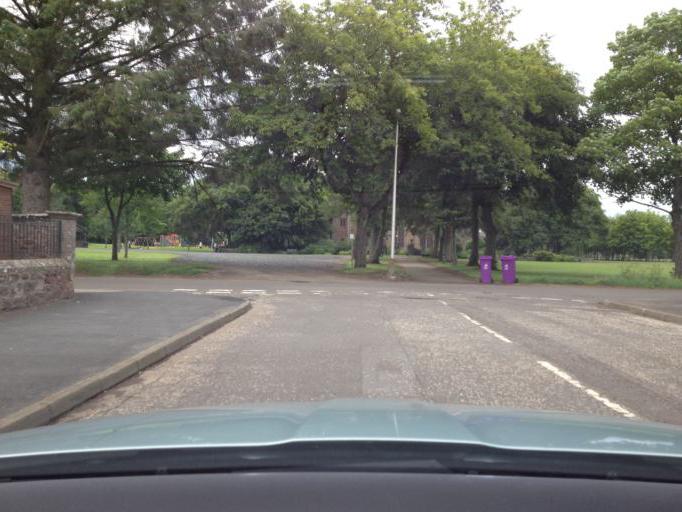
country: GB
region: Scotland
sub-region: Angus
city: Brechin
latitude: 56.8115
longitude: -2.6587
